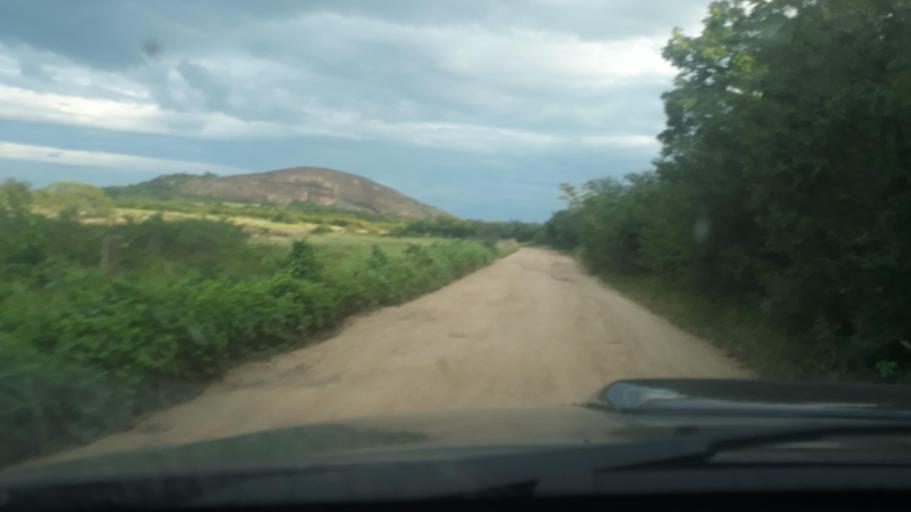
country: BR
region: Bahia
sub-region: Riacho De Santana
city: Riacho de Santana
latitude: -13.9111
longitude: -42.9495
